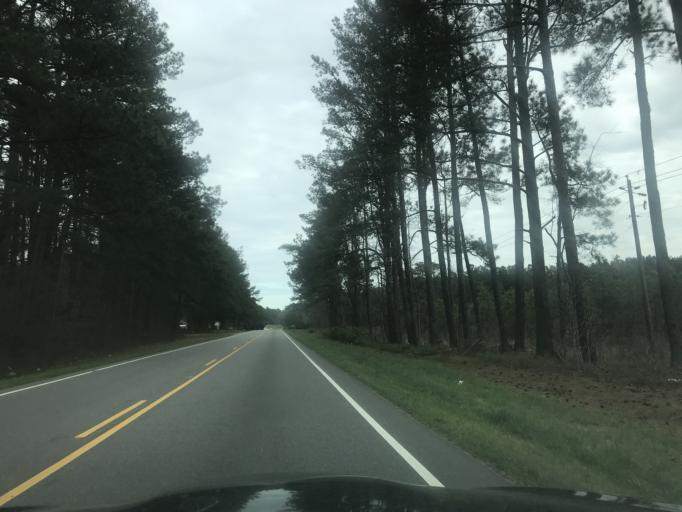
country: US
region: North Carolina
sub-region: Franklin County
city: Franklinton
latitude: 36.0991
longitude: -78.4245
